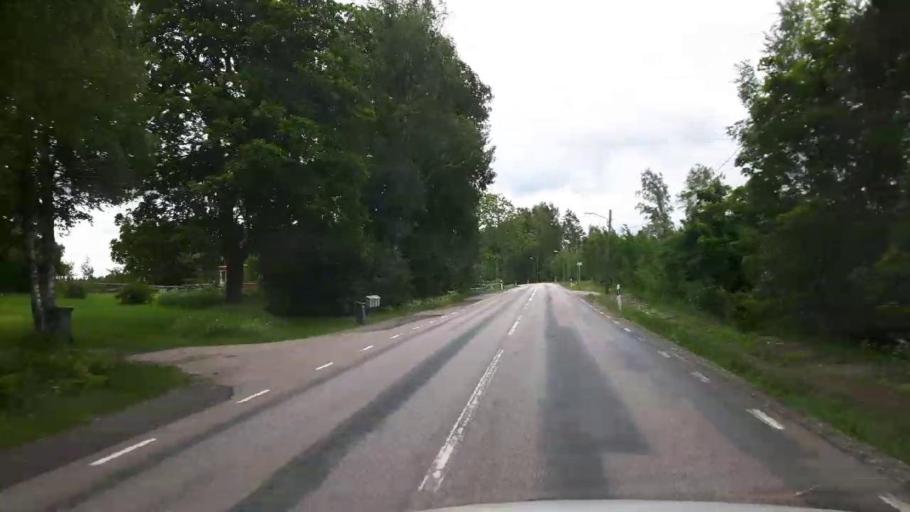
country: SE
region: Vaestmanland
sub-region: Kopings Kommun
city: Kolsva
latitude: 59.6304
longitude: 15.8047
